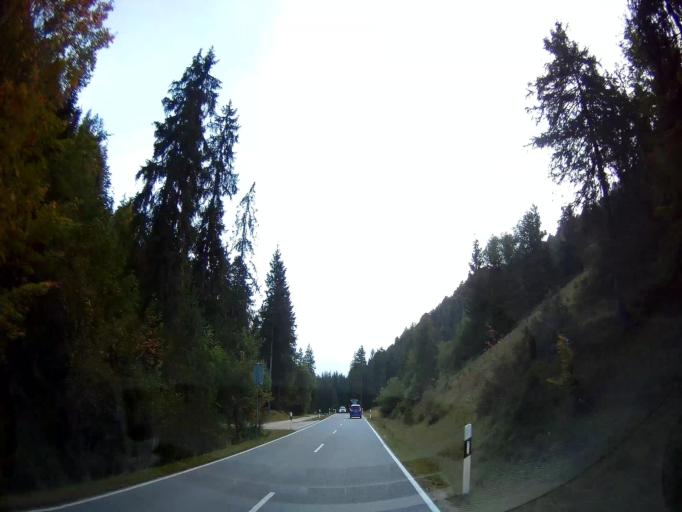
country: DE
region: Bavaria
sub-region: Upper Bavaria
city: Ramsau
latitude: 47.6352
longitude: 12.9105
